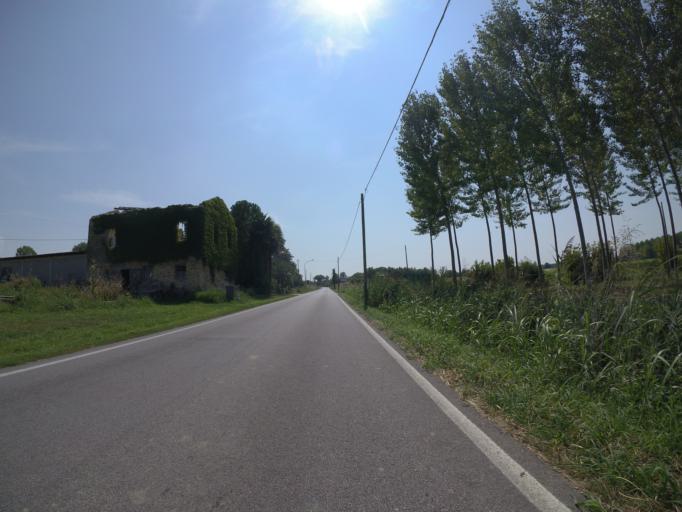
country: IT
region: Friuli Venezia Giulia
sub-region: Provincia di Udine
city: Pocenia
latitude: 45.8458
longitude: 13.0947
